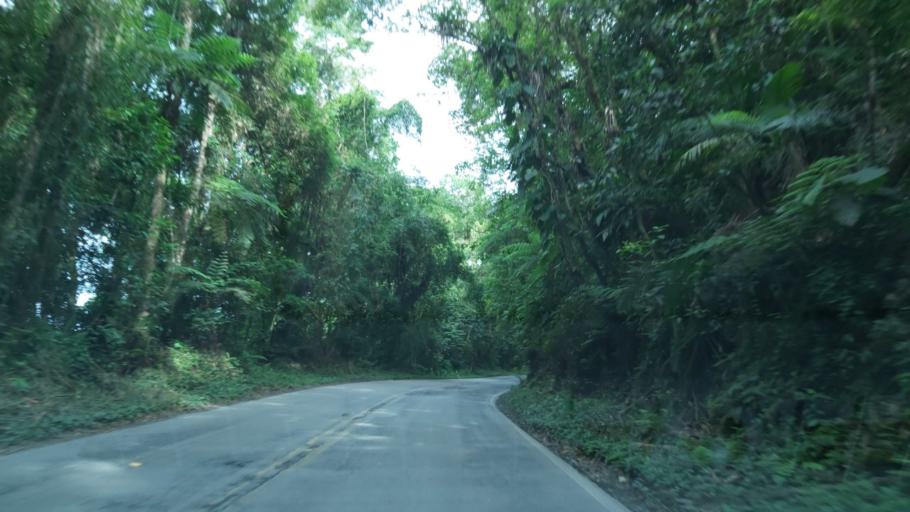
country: BR
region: Sao Paulo
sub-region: Miracatu
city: Miracatu
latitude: -24.0537
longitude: -47.5709
